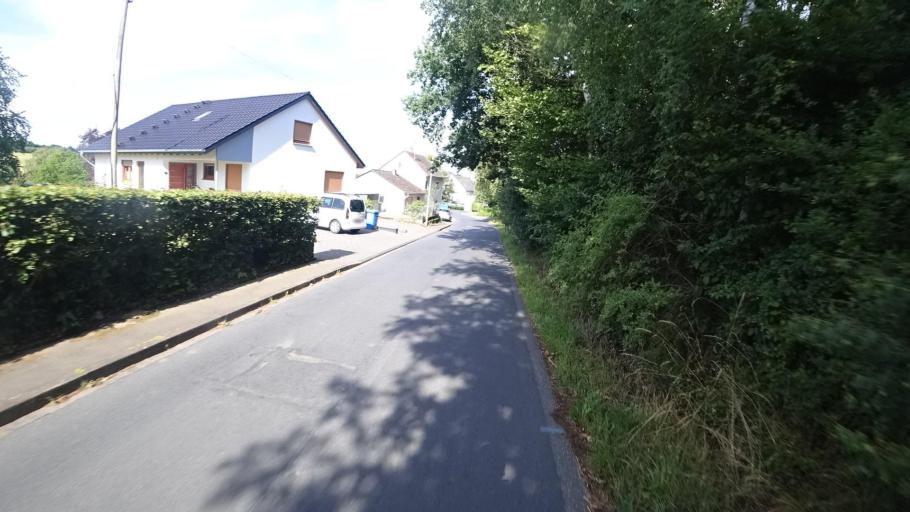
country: DE
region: Rheinland-Pfalz
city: Oberwambach
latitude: 50.6584
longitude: 7.6596
